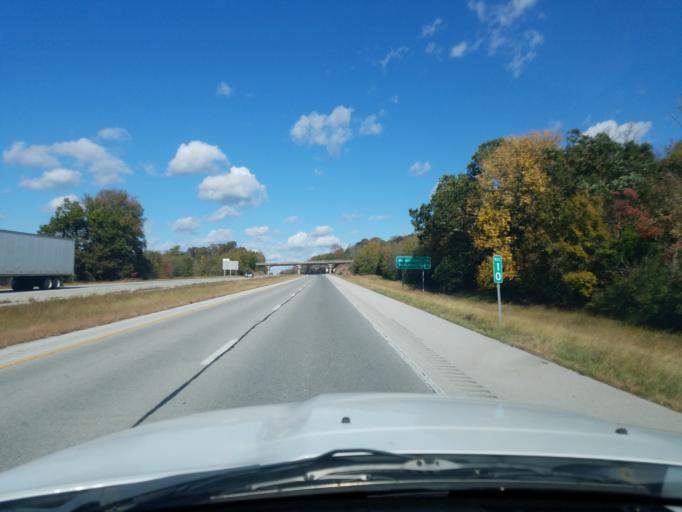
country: US
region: Kentucky
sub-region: Warren County
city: Bowling Green
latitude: 36.9996
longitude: -86.5059
